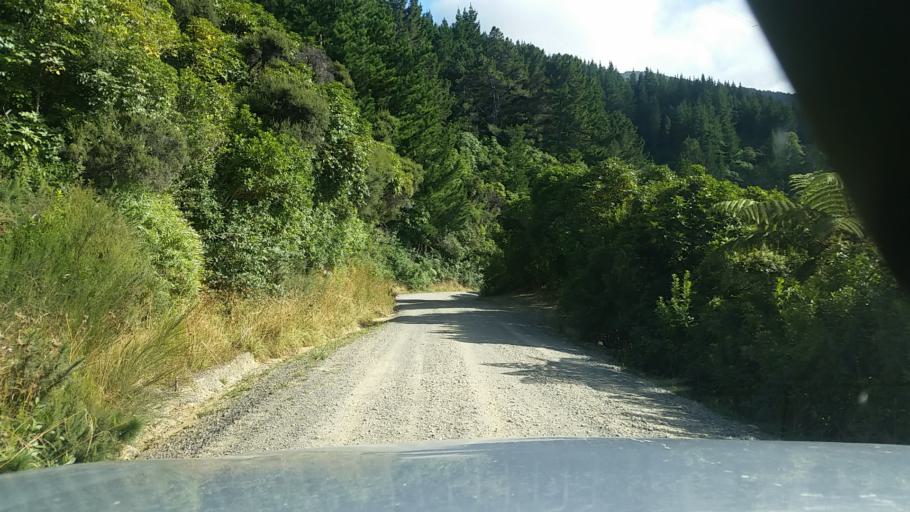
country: NZ
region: Marlborough
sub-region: Marlborough District
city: Picton
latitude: -41.2892
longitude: 174.1310
